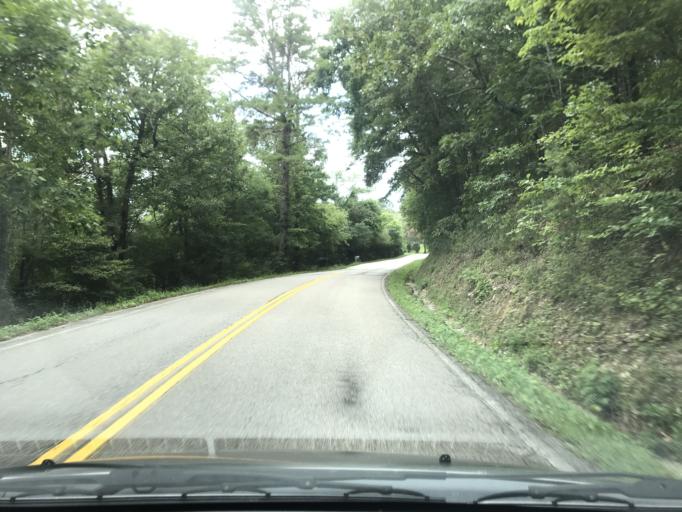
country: US
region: Tennessee
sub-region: Hamilton County
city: Lakesite
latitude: 35.1674
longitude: -85.0843
